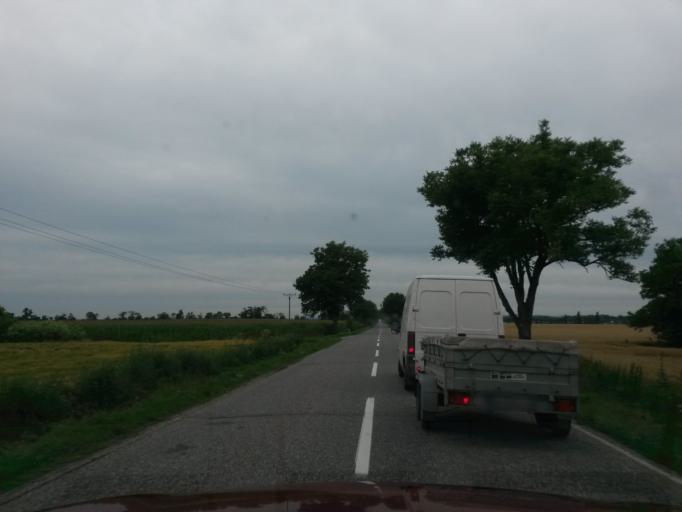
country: SK
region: Nitriansky
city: Levice
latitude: 48.1422
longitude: 18.5826
